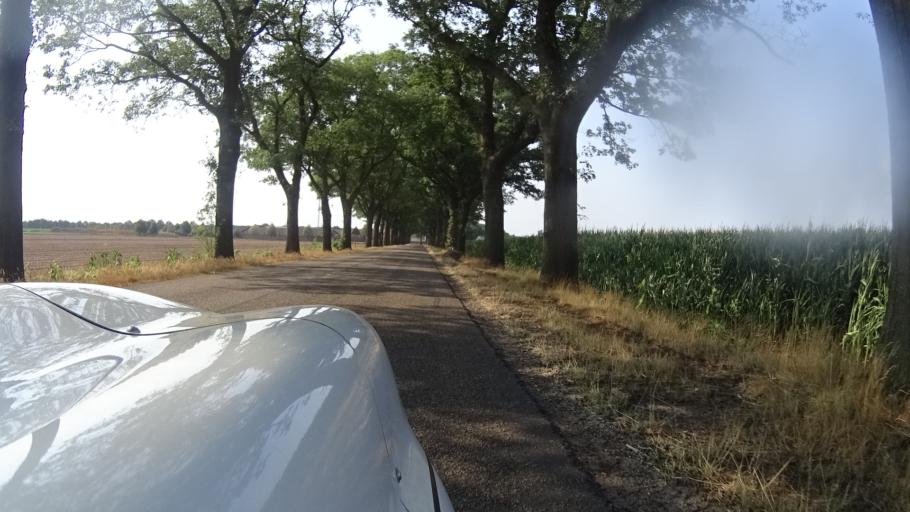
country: NL
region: North Brabant
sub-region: Gemeente Mill en Sint Hubert
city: Wilbertoord
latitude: 51.6257
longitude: 5.7950
